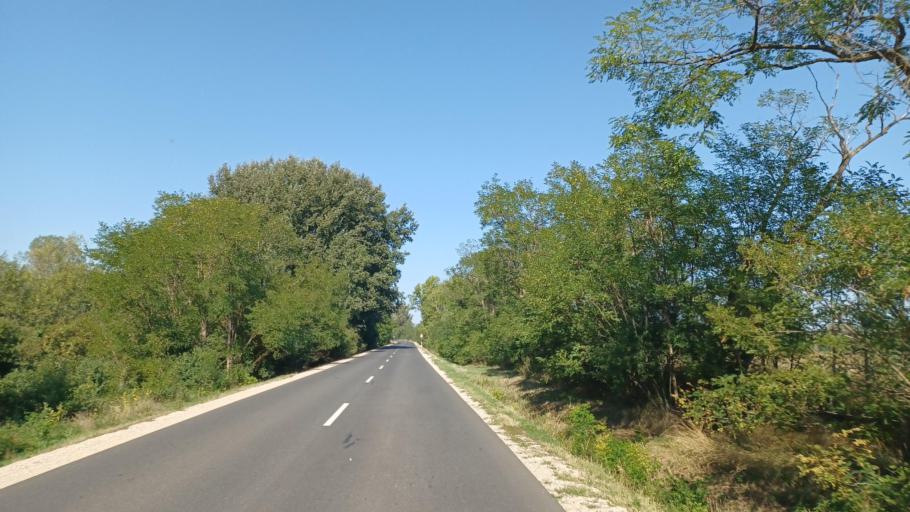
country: HU
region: Fejer
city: Alap
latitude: 46.7432
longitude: 18.6964
